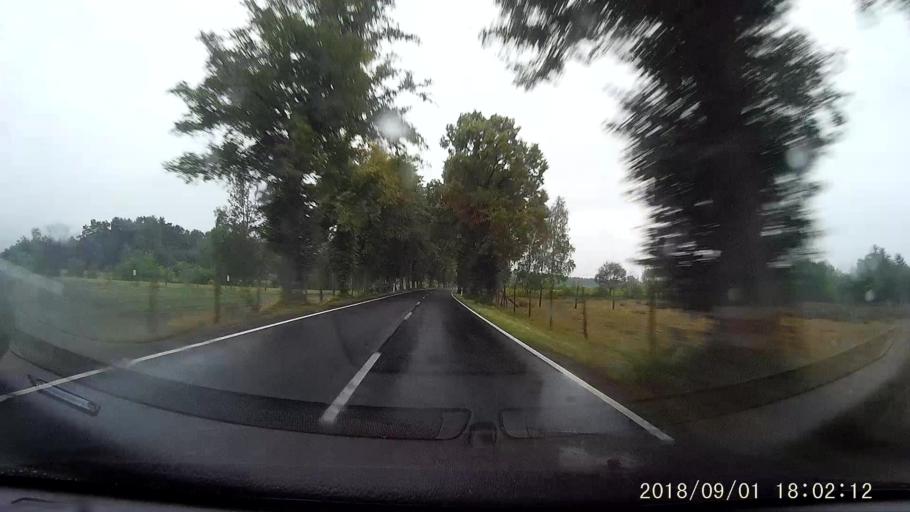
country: PL
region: Lubusz
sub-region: Powiat zaganski
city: Gozdnica
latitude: 51.3892
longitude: 15.1781
